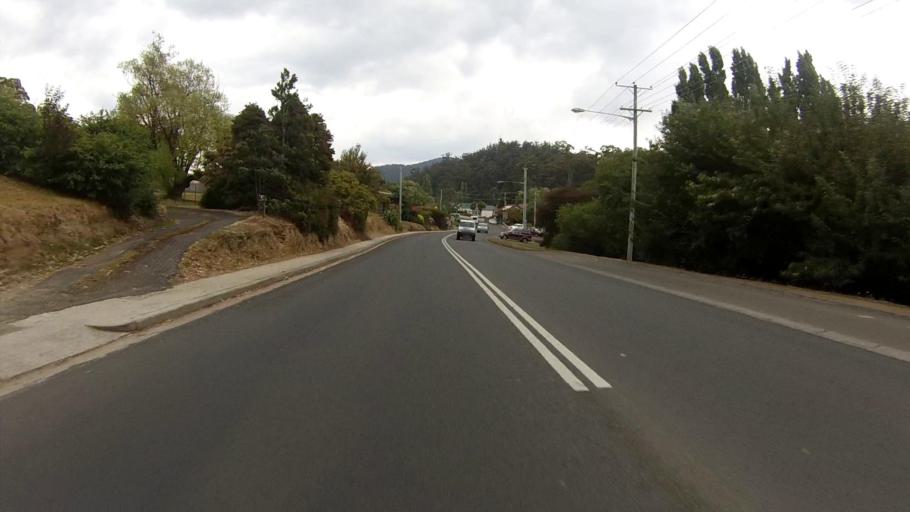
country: AU
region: Tasmania
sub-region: Huon Valley
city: Cygnet
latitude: -43.1567
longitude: 147.0742
